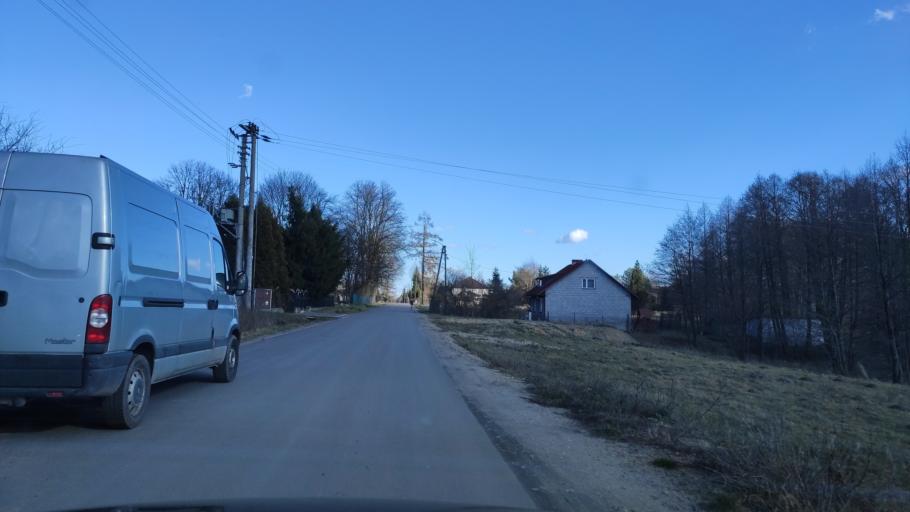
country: PL
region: Masovian Voivodeship
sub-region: Powiat radomski
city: Jedlnia-Letnisko
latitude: 51.4399
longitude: 21.2963
